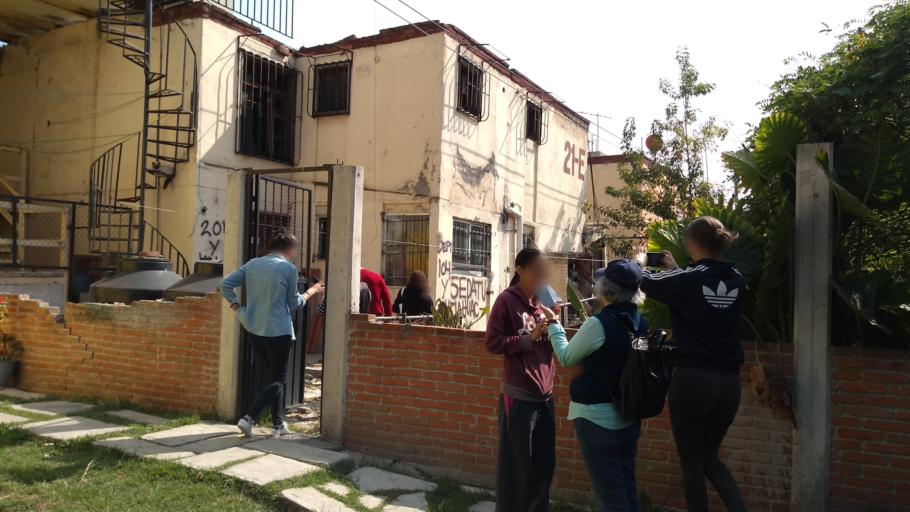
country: MX
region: Mexico City
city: Tlahuac
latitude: 19.2869
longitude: -99.0534
